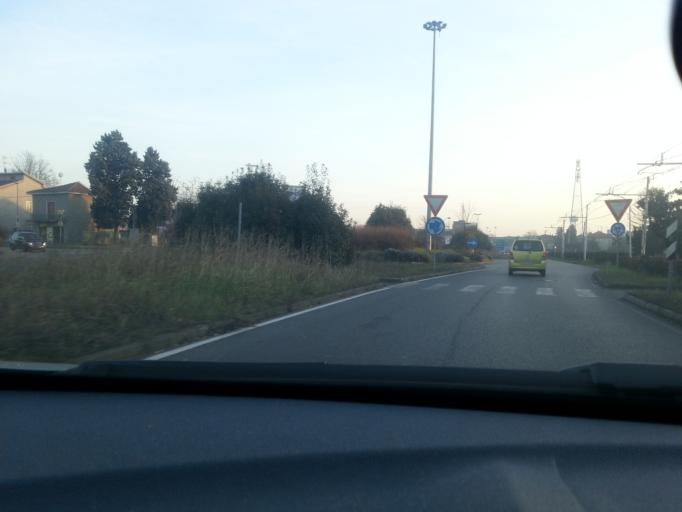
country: IT
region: Lombardy
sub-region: Citta metropolitana di Milano
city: Cormano
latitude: 45.5385
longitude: 9.1597
